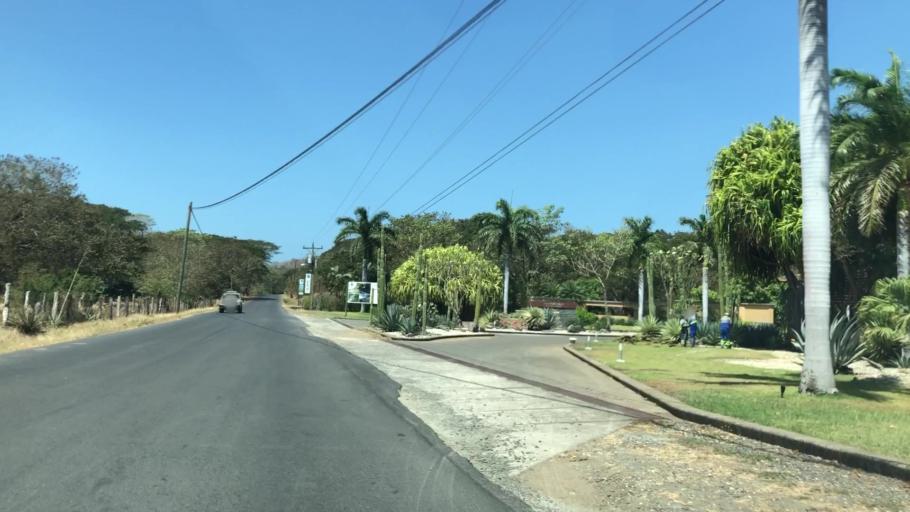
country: CR
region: Guanacaste
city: Sardinal
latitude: 10.3456
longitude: -85.8347
